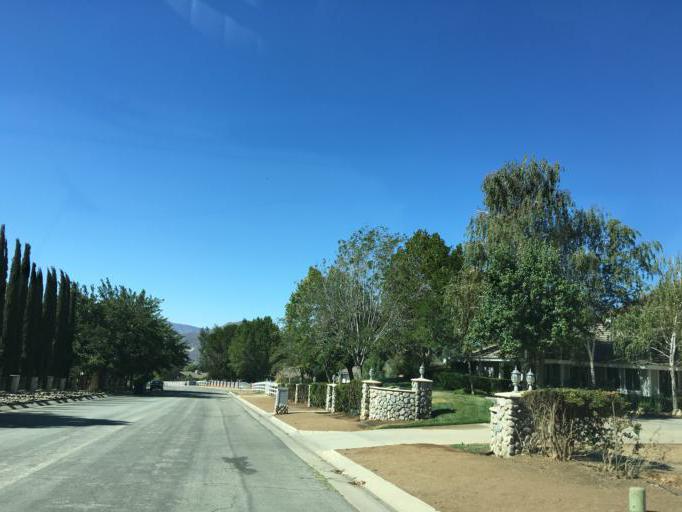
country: US
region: California
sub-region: Los Angeles County
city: Acton
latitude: 34.5039
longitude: -118.1964
